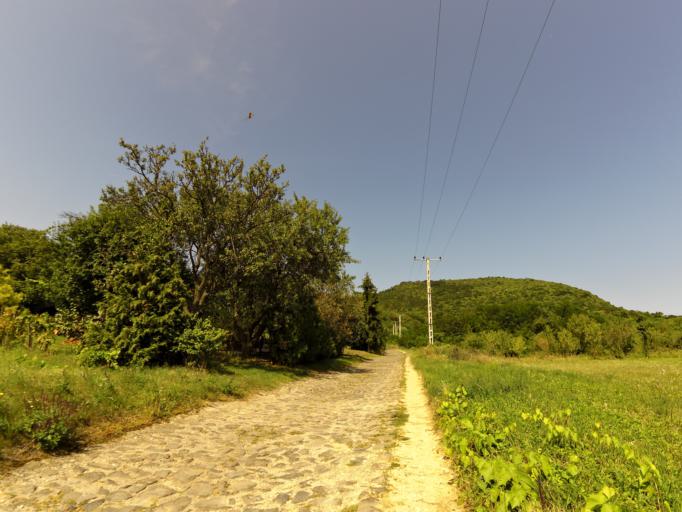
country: HU
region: Zala
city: Vonyarcvashegy
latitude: 46.7884
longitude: 17.3696
